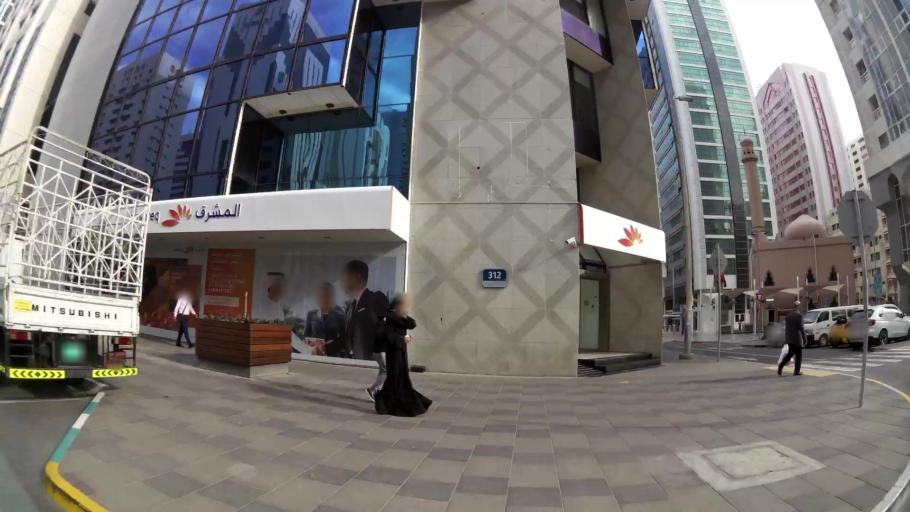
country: AE
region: Abu Dhabi
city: Abu Dhabi
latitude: 24.4906
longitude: 54.3595
